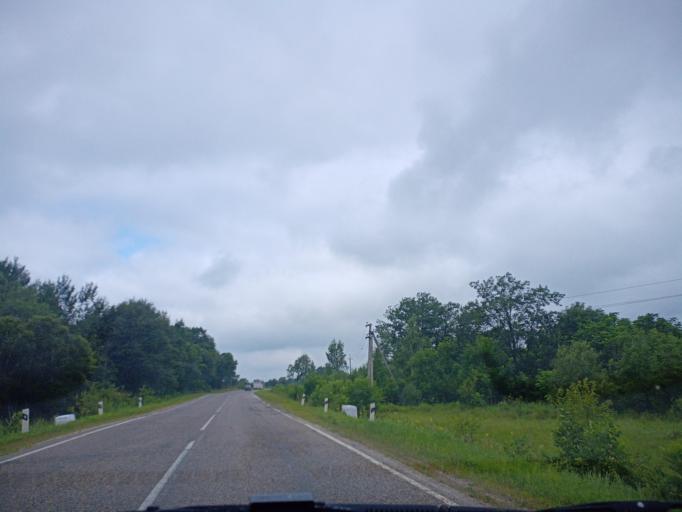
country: RU
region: Primorskiy
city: Novopokrovka
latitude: 45.9712
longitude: 134.2296
